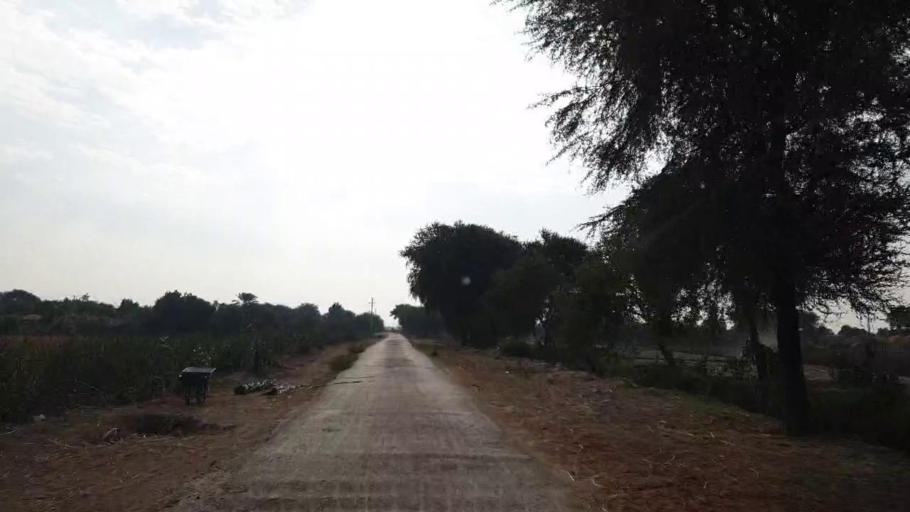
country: PK
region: Sindh
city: Tando Muhammad Khan
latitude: 25.0356
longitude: 68.4365
